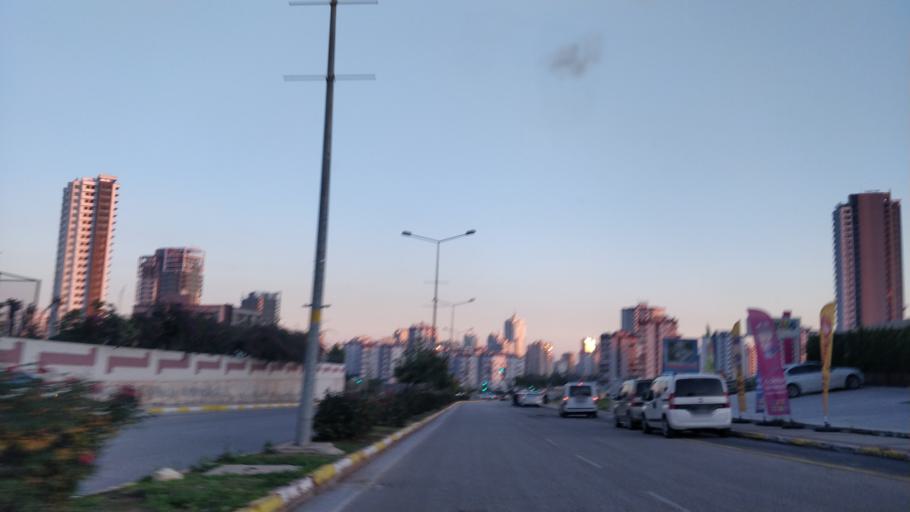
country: TR
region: Mersin
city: Mercin
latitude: 36.7986
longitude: 34.5759
